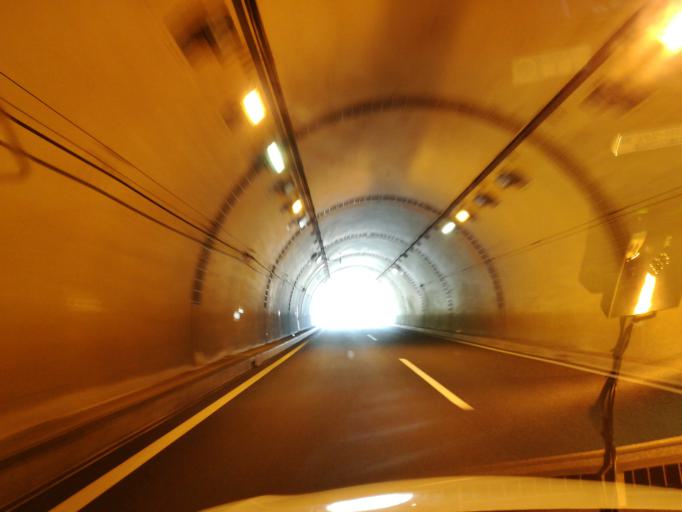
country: JP
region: Ehime
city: Kawanoecho
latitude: 33.8281
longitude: 133.6600
